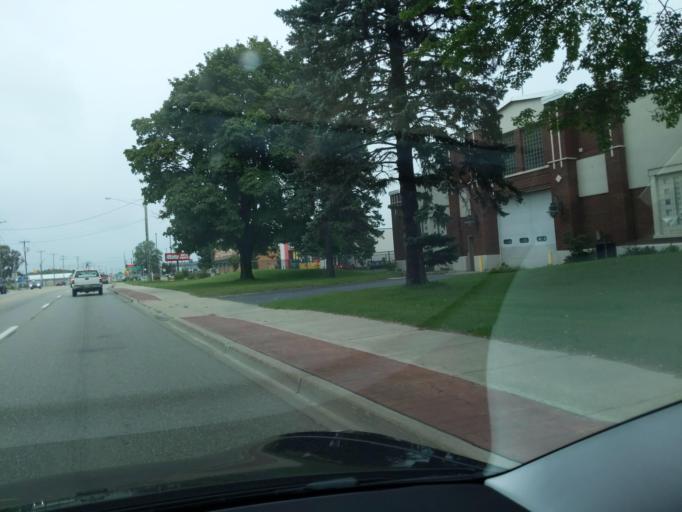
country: US
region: Michigan
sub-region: Wexford County
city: Cadillac
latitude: 44.2650
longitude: -85.4060
